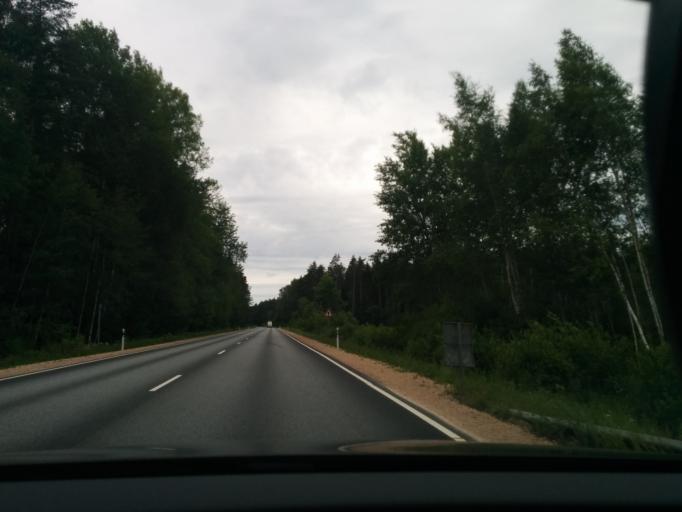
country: LV
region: Ikskile
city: Ikskile
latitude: 56.8731
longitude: 24.5358
